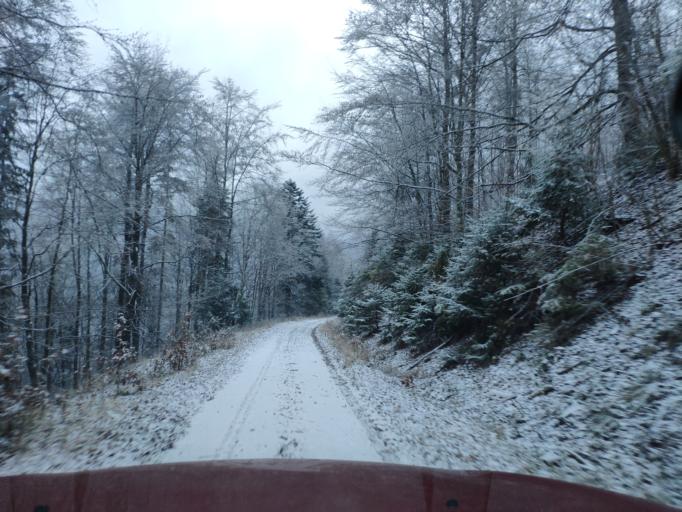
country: SK
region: Kosicky
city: Dobsina
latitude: 48.8123
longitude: 20.5047
